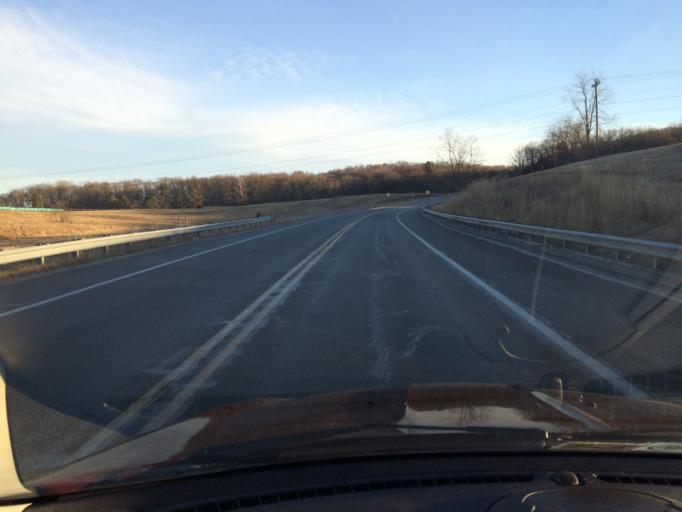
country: US
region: Virginia
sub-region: City of Staunton
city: Staunton
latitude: 38.1810
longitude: -79.0958
